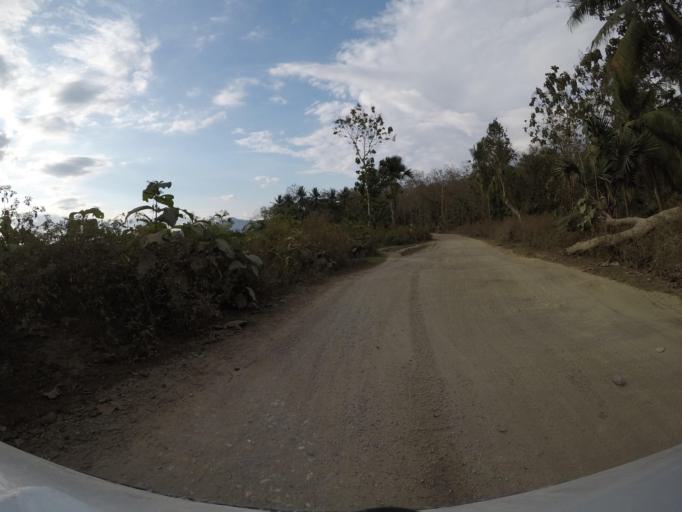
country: TL
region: Bobonaro
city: Maliana
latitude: -8.8891
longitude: 125.2091
